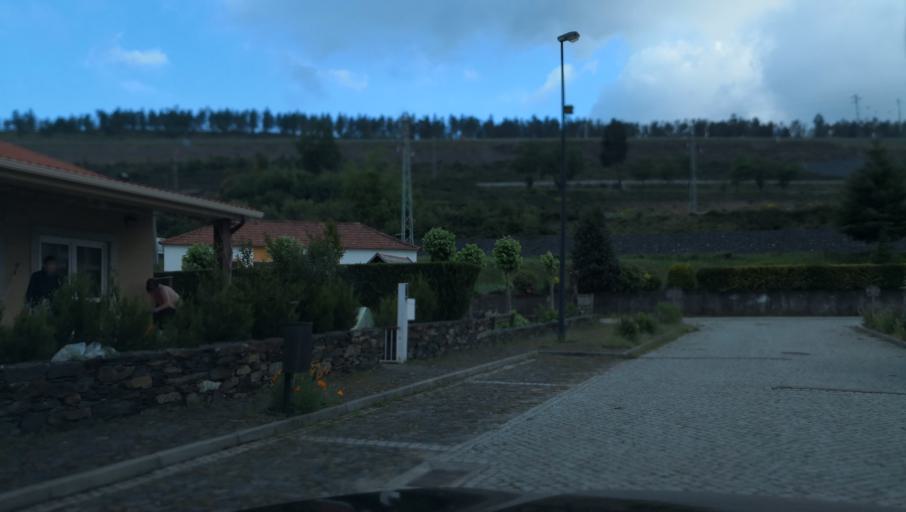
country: PT
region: Vila Real
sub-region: Santa Marta de Penaguiao
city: Santa Marta de Penaguiao
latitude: 41.2821
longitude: -7.8466
